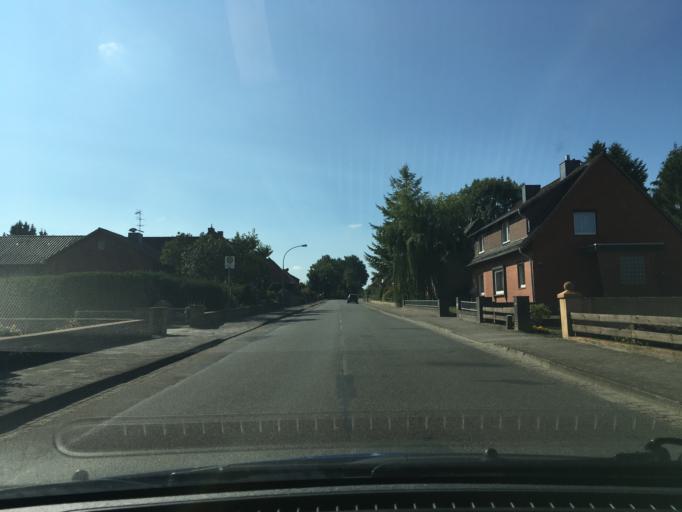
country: DE
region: Lower Saxony
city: Wriedel
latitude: 53.0294
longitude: 10.2829
